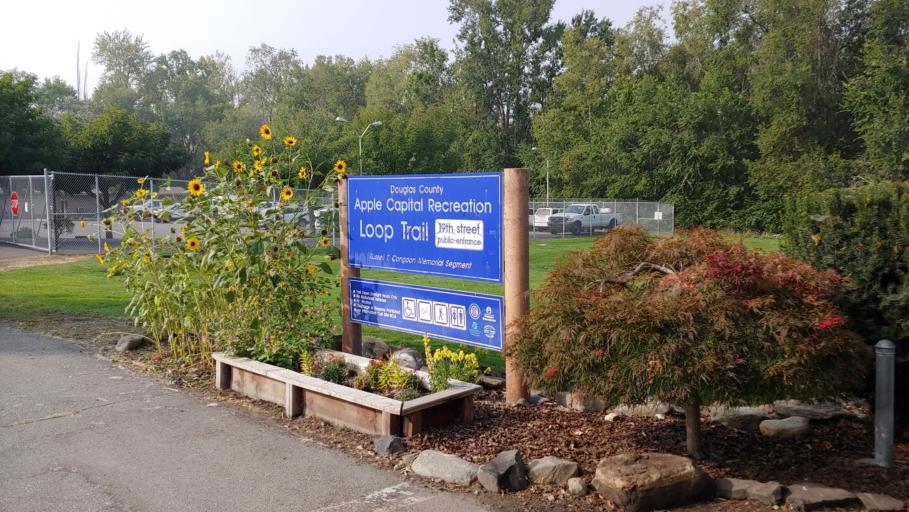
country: US
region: Washington
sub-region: Chelan County
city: Wenatchee
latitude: 47.4339
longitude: -120.3019
